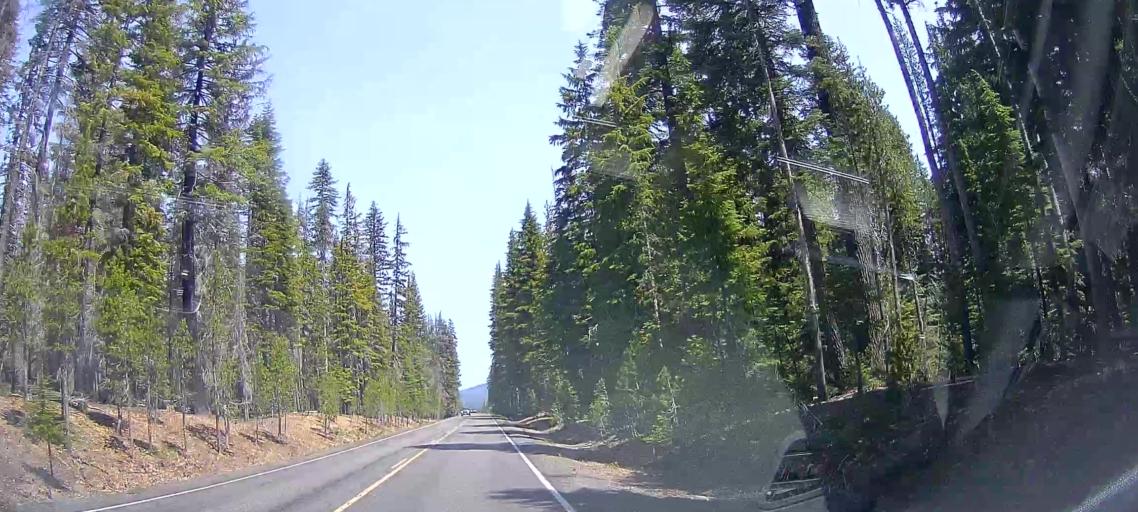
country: US
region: Oregon
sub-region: Lane County
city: Oakridge
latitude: 43.0647
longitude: -122.1203
